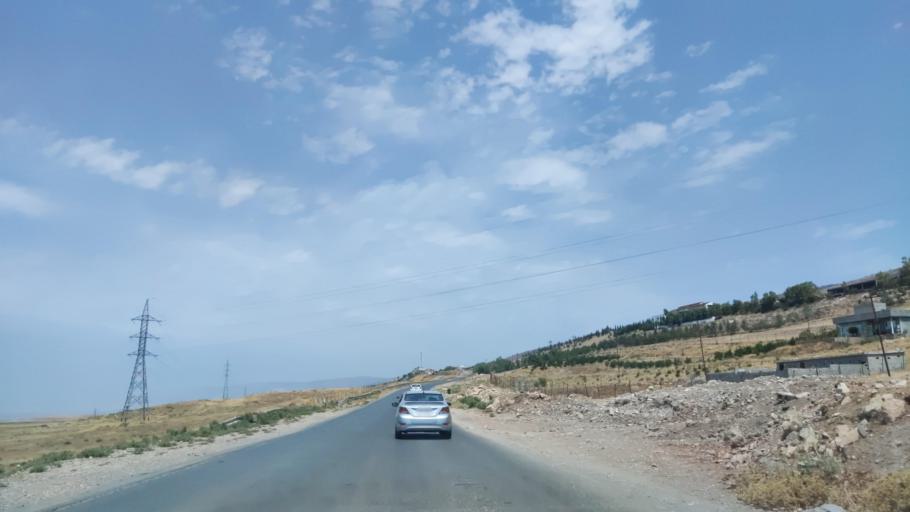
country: IQ
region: Arbil
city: Shaqlawah
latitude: 36.5370
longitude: 44.3519
